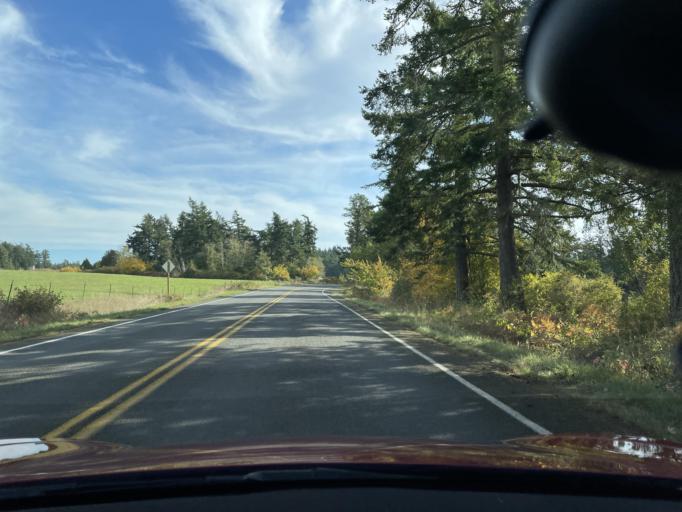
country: US
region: Washington
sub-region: San Juan County
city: Friday Harbor
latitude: 48.6105
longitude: -123.1437
